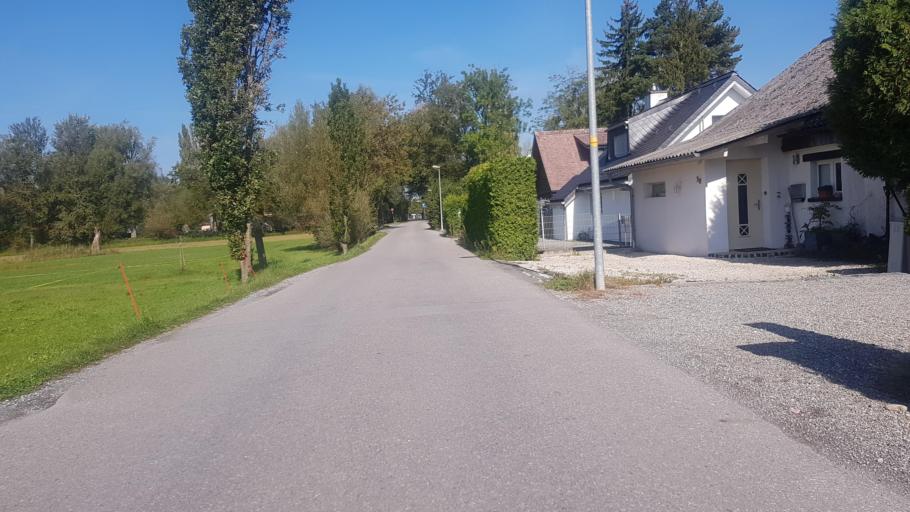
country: CH
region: Saint Gallen
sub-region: Wahlkreis Rheintal
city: Rheineck
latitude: 47.4957
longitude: 9.5615
